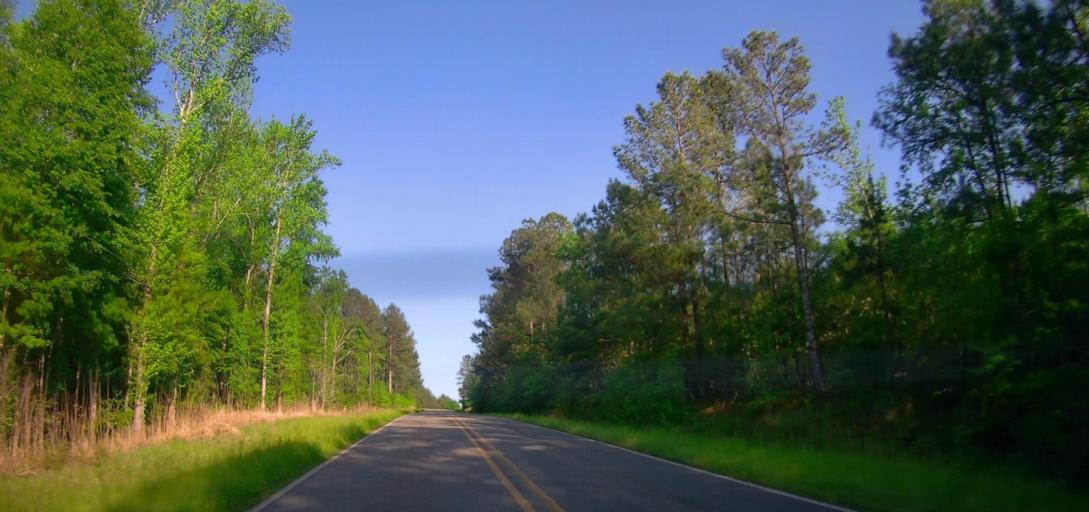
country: US
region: Georgia
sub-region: Putnam County
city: Eatonton
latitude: 33.2838
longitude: -83.3207
